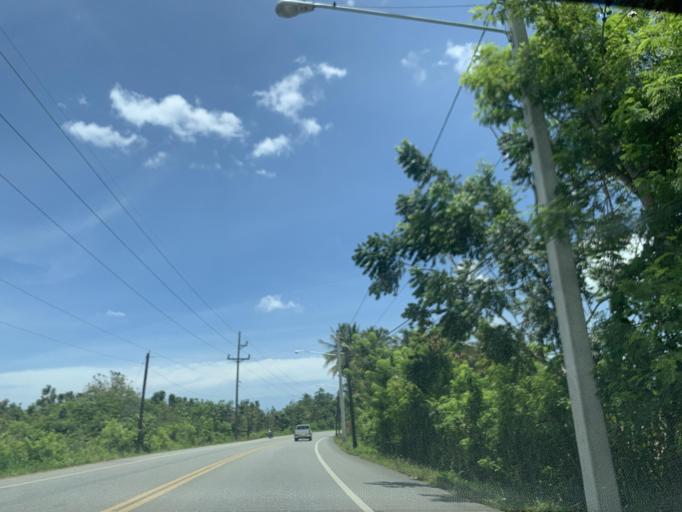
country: DO
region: Puerto Plata
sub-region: Puerto Plata
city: Puerto Plata
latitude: 19.7476
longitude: -70.5974
